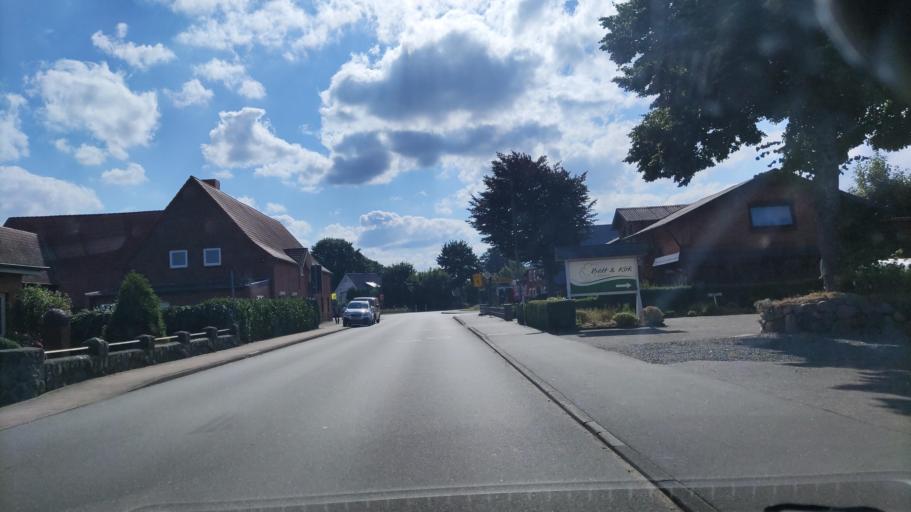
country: DE
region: Schleswig-Holstein
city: Alt Duvenstedt
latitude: 54.3583
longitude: 9.6432
